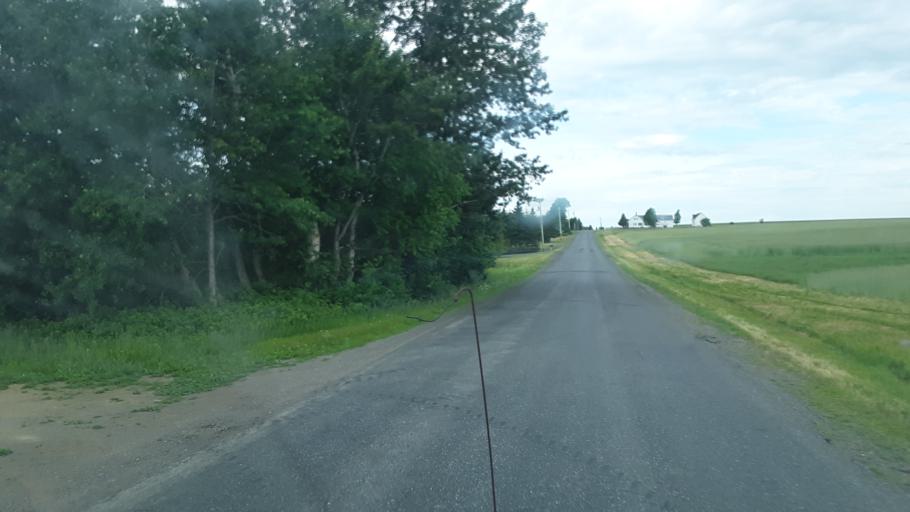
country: US
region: Maine
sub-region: Aroostook County
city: Caribou
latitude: 46.8113
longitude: -68.0082
